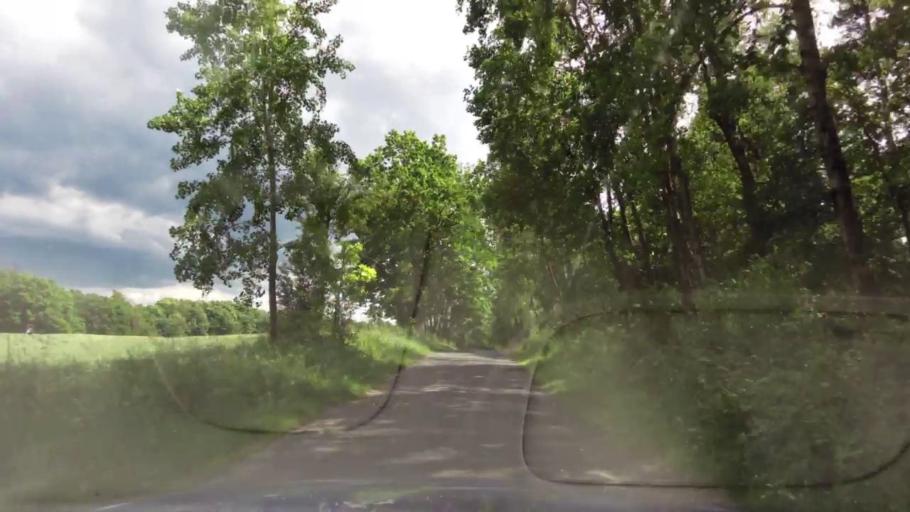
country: PL
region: West Pomeranian Voivodeship
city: Trzcinsko Zdroj
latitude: 52.9014
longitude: 14.6084
